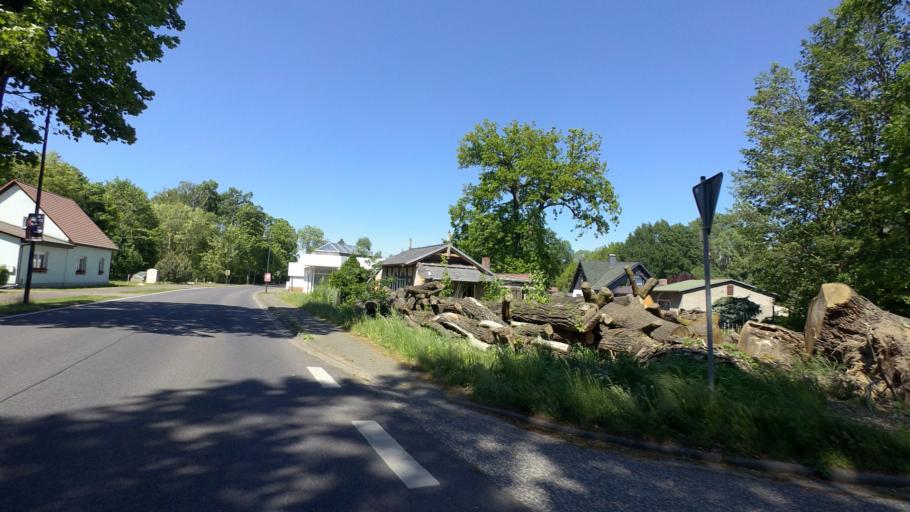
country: DE
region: Brandenburg
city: Lieberose
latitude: 51.9751
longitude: 14.3026
